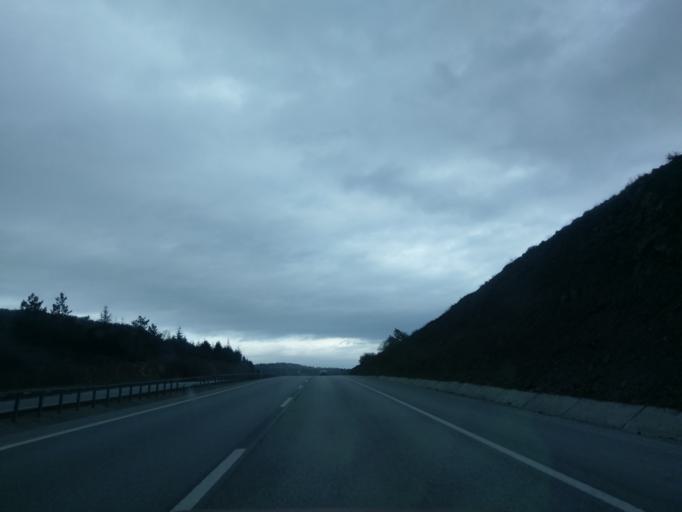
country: TR
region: Kuetahya
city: Sabuncu
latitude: 39.5783
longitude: 30.1206
